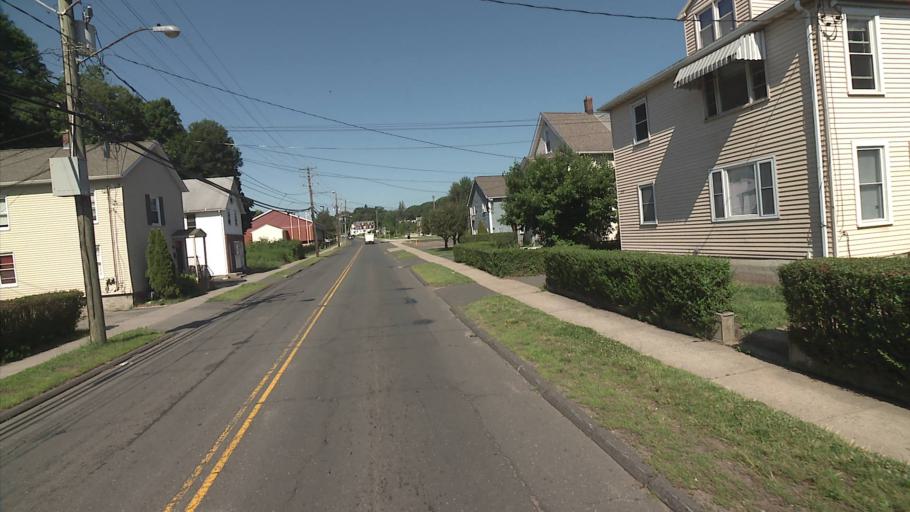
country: US
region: Connecticut
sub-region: Hartford County
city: Bristol
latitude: 41.6725
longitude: -72.9576
